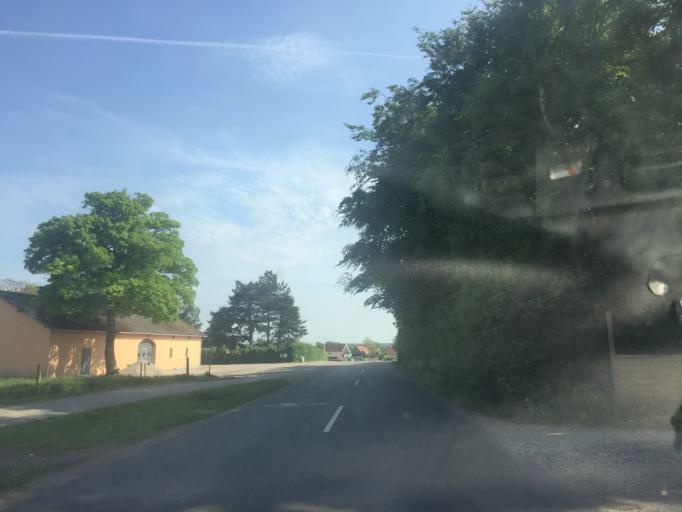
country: DK
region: Capital Region
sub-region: Egedal Kommune
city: Smorumnedre
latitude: 55.7143
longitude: 12.2969
